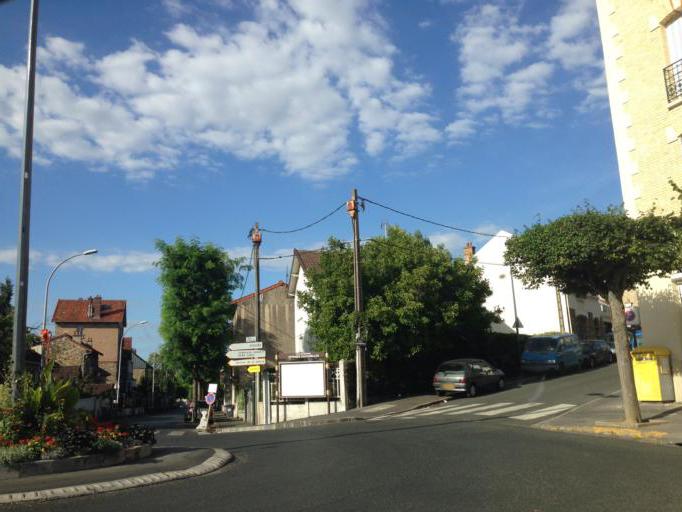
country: FR
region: Ile-de-France
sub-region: Departement des Hauts-de-Seine
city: Meudon
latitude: 48.8037
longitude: 2.2395
